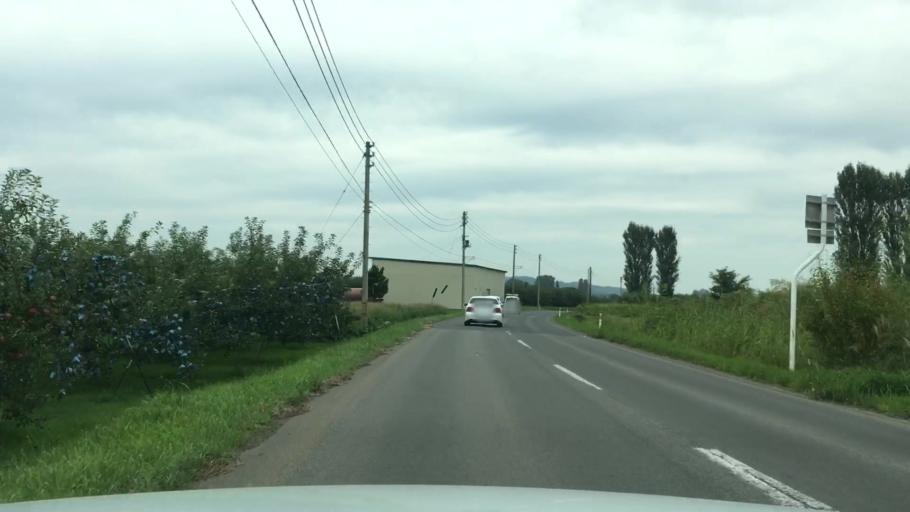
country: JP
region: Aomori
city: Hirosaki
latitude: 40.6455
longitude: 140.4247
